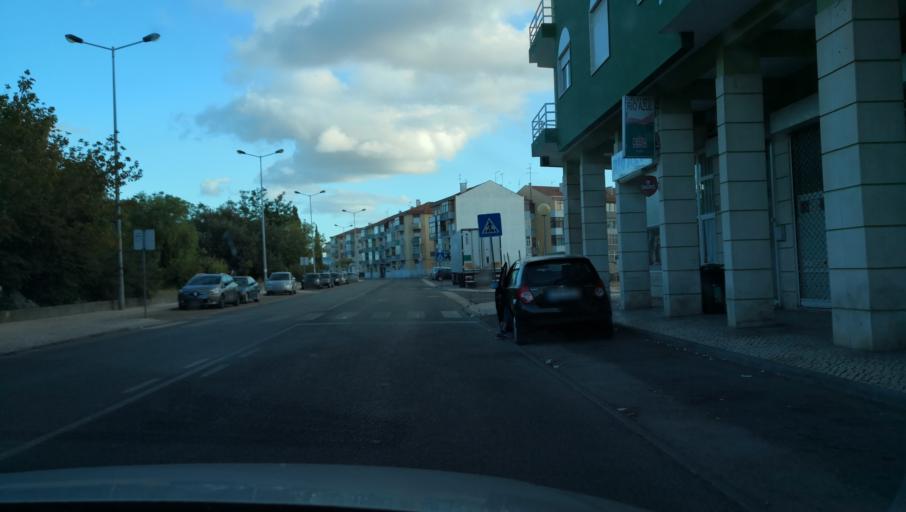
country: PT
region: Setubal
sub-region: Moita
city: Alhos Vedros
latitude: 38.6608
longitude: -9.0420
